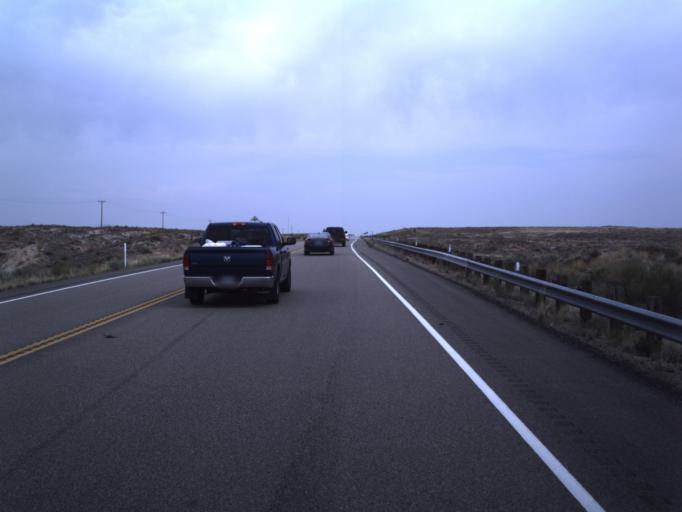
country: US
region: Arizona
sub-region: Coconino County
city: Page
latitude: 37.1042
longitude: -111.8572
